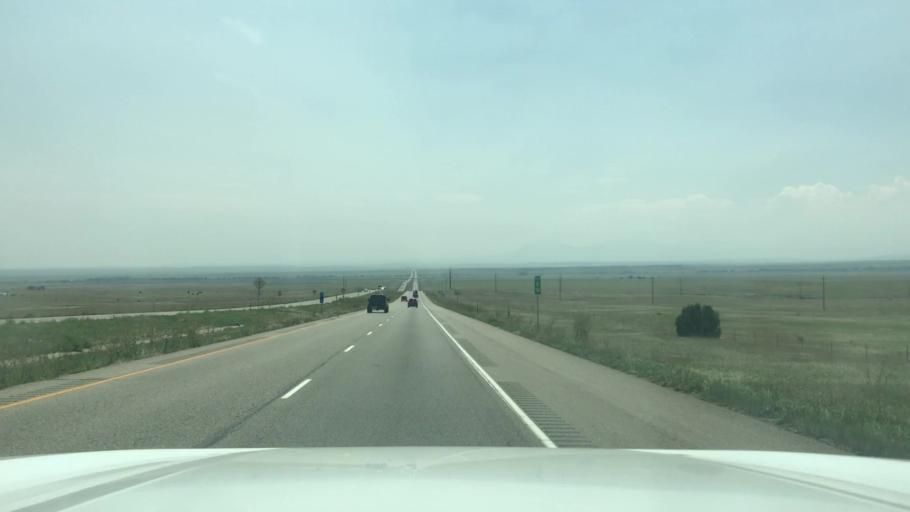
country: US
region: Colorado
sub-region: Pueblo County
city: Colorado City
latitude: 37.8940
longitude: -104.8293
